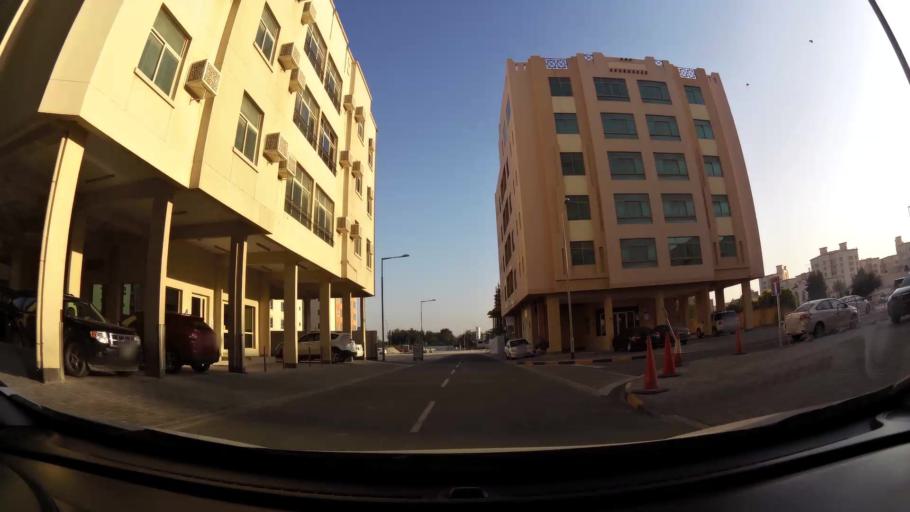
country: BH
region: Manama
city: Jidd Hafs
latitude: 26.2260
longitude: 50.5544
